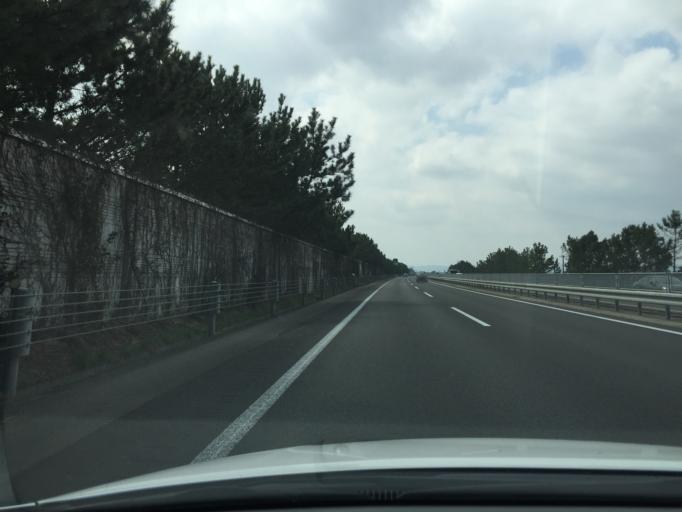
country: JP
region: Miyagi
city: Iwanuma
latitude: 38.1727
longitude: 140.9223
